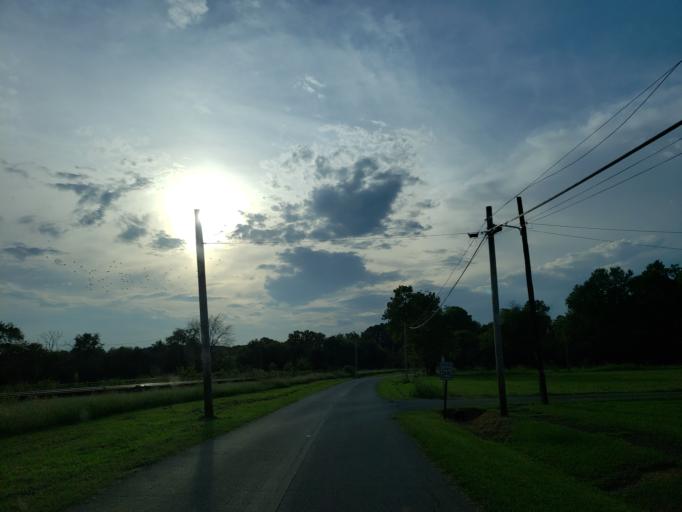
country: US
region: Georgia
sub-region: Bartow County
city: Euharlee
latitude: 34.2370
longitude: -84.9476
